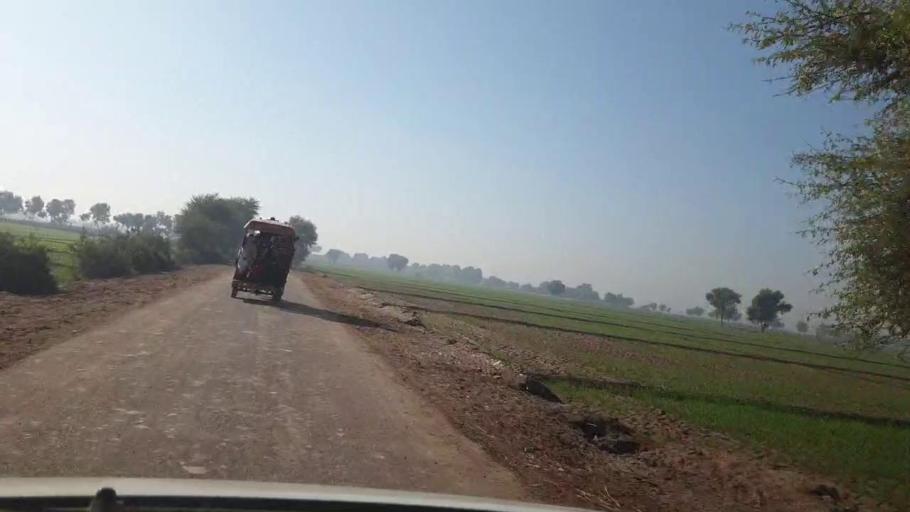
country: PK
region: Sindh
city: Dadu
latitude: 26.6454
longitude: 67.8216
